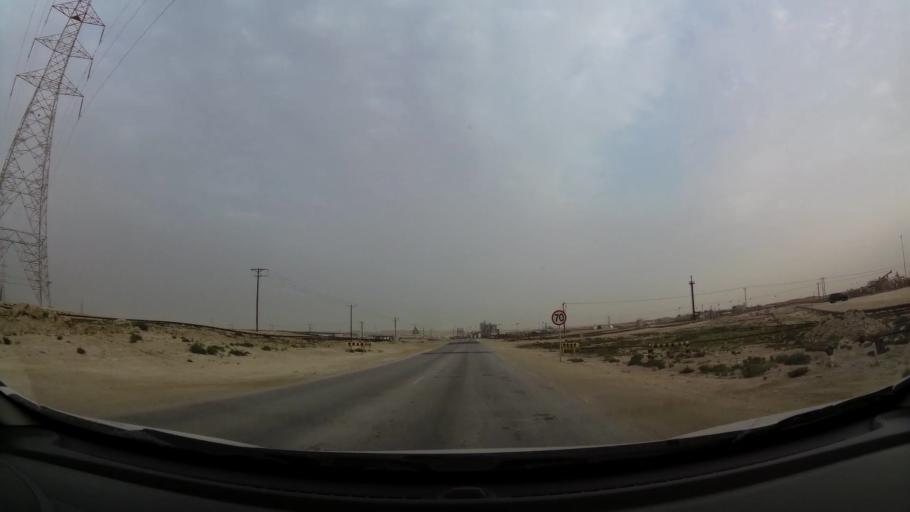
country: BH
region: Central Governorate
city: Dar Kulayb
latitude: 26.0193
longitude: 50.5728
